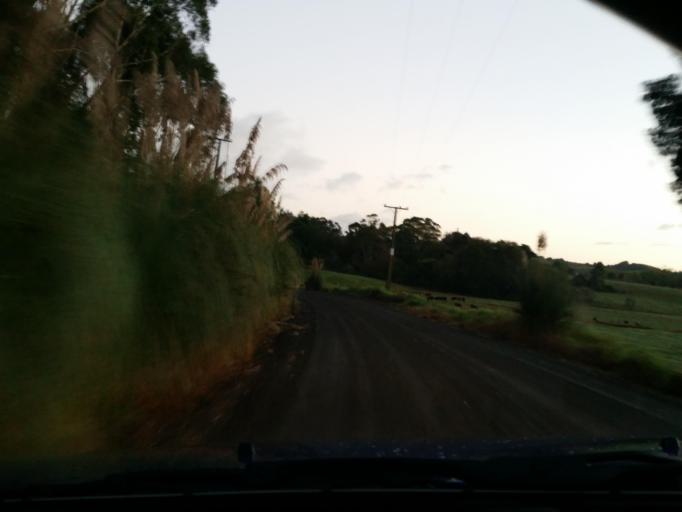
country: NZ
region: Northland
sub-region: Whangarei
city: Maungatapere
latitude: -35.8191
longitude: 174.0403
